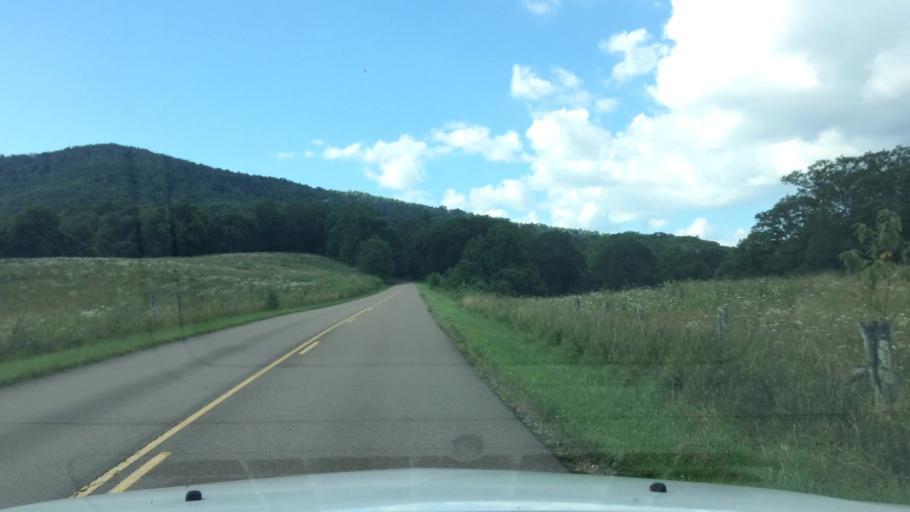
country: US
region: North Carolina
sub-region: Watauga County
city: Blowing Rock
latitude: 36.1512
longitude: -81.6664
